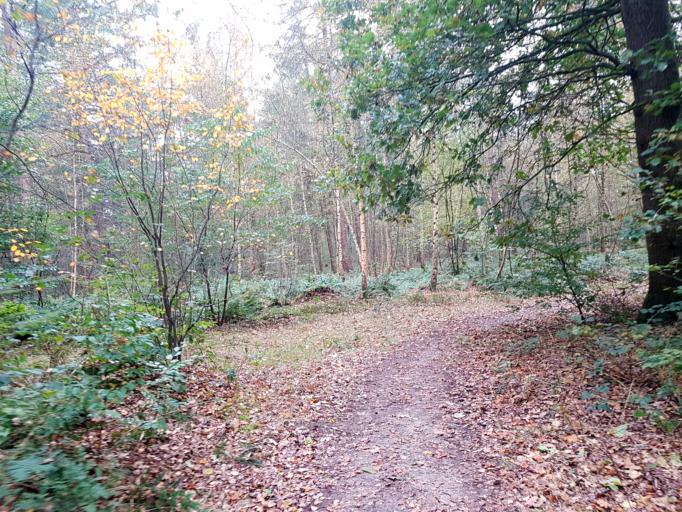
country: NL
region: Utrecht
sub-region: Gemeente Utrechtse Heuvelrug
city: Maarsbergen
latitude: 52.0263
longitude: 5.3935
